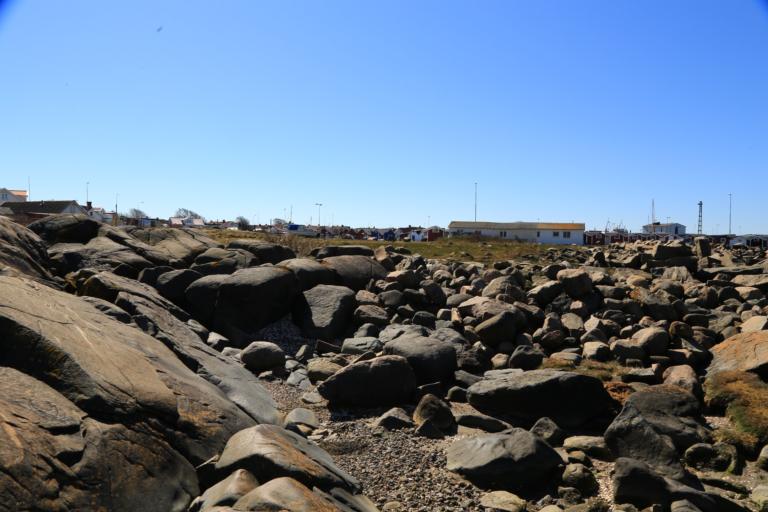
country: SE
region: Halland
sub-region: Varbergs Kommun
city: Traslovslage
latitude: 57.0608
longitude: 12.2746
